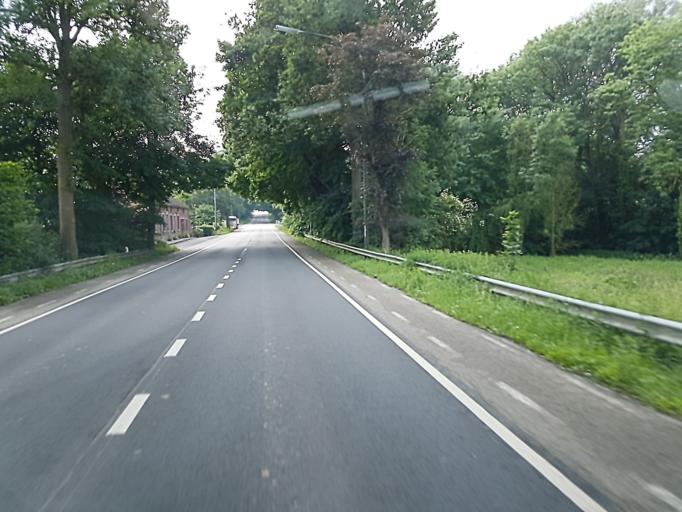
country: BE
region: Wallonia
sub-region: Province du Hainaut
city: Soignies
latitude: 50.6163
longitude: 4.0550
